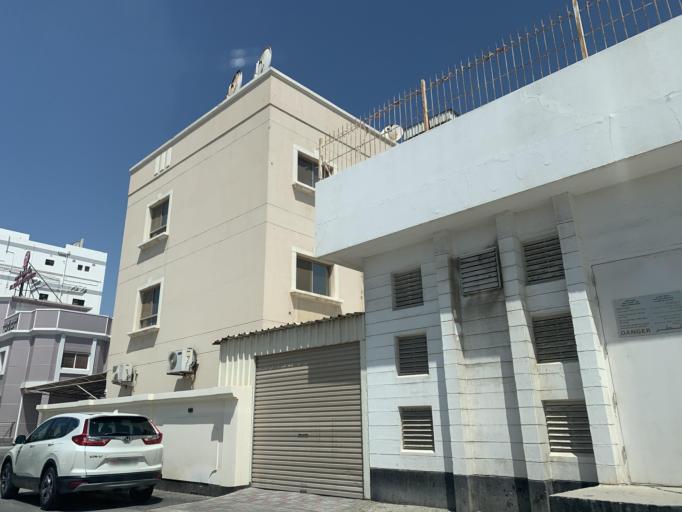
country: BH
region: Manama
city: Manama
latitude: 26.2089
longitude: 50.5740
